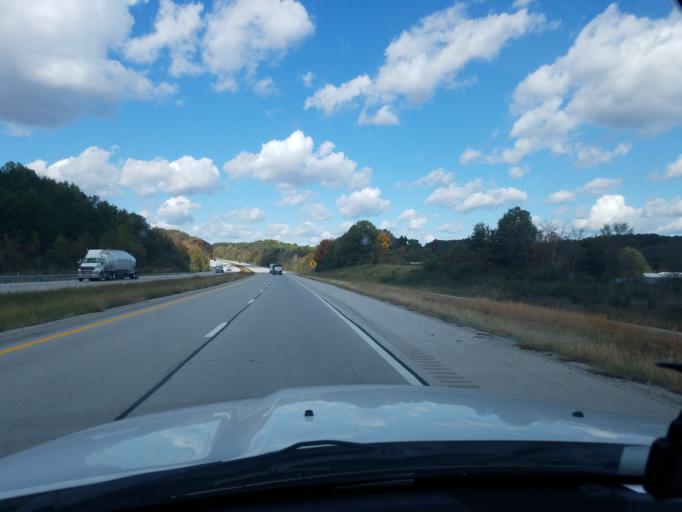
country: US
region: Kentucky
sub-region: Butler County
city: Morgantown
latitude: 37.2163
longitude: -86.7120
